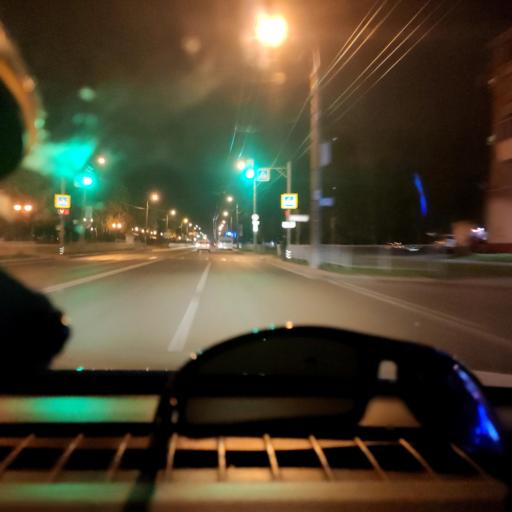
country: RU
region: Samara
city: Samara
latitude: 53.2313
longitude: 50.2126
